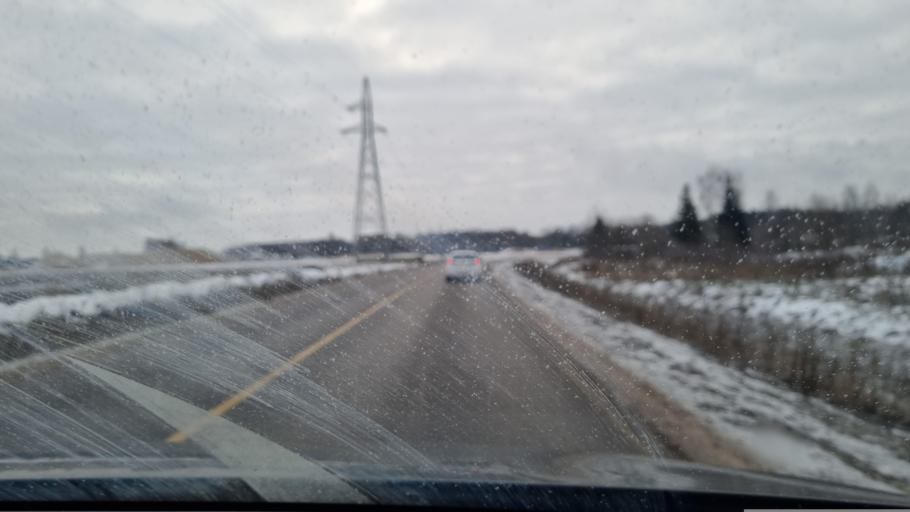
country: LV
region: Kekava
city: Balozi
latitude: 56.8743
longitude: 24.1649
